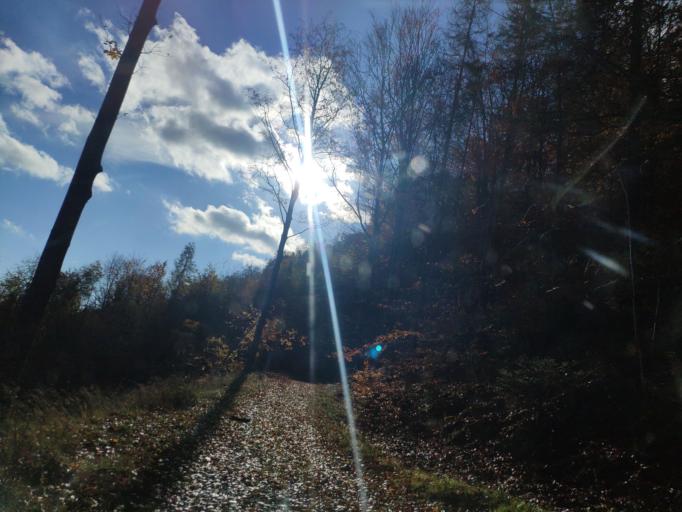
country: SK
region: Kosicky
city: Moldava nad Bodvou
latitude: 48.7411
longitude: 21.0185
